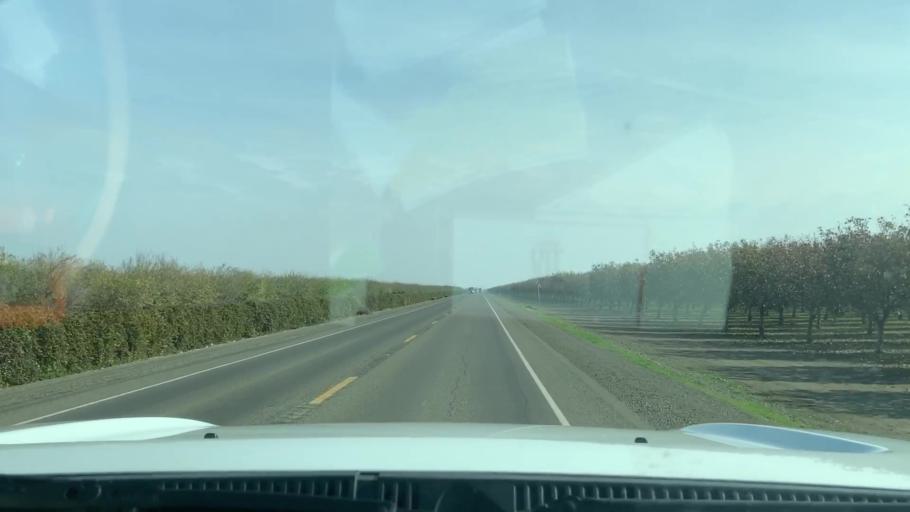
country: US
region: California
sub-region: Fresno County
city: Huron
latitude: 36.2553
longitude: -120.1185
